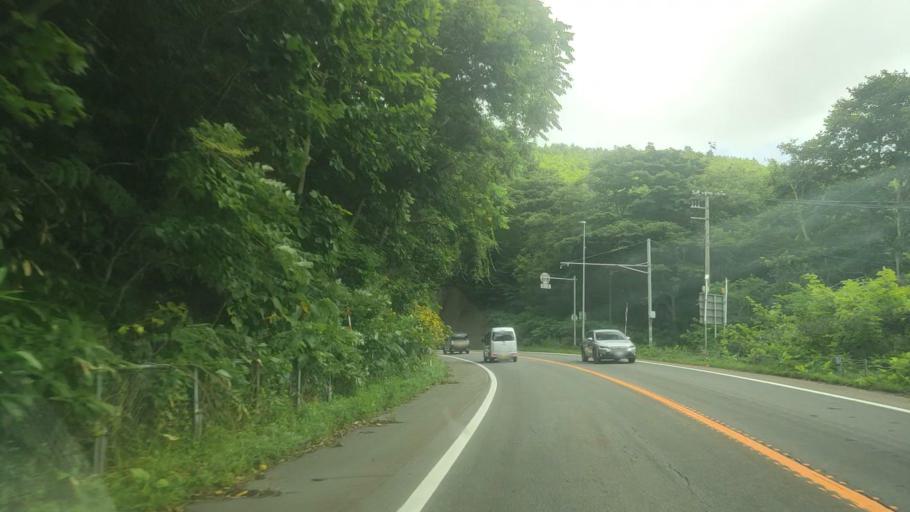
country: JP
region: Hokkaido
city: Niseko Town
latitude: 42.5933
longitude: 140.5980
